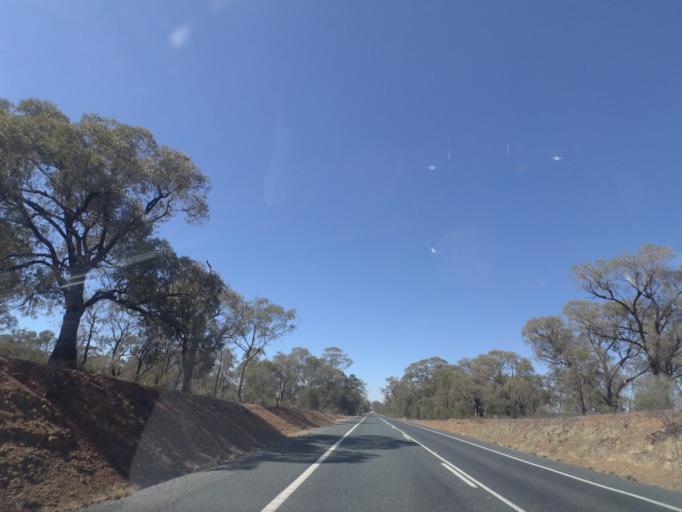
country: AU
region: New South Wales
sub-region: Bland
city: West Wyalong
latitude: -34.1676
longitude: 147.1156
